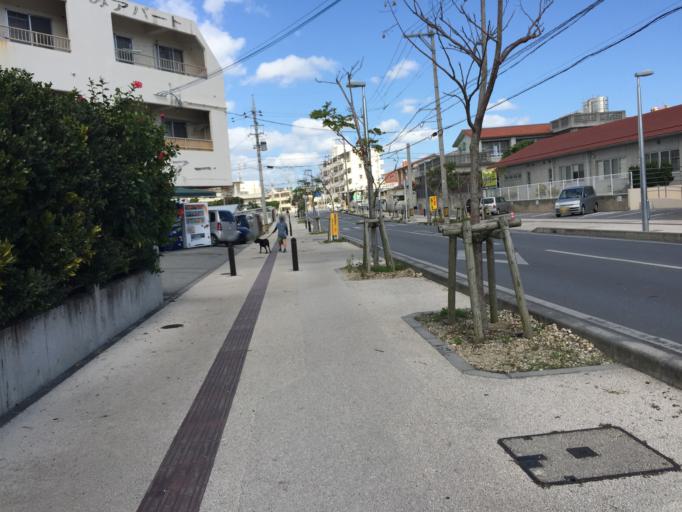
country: JP
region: Okinawa
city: Ginowan
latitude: 26.2325
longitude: 127.7338
